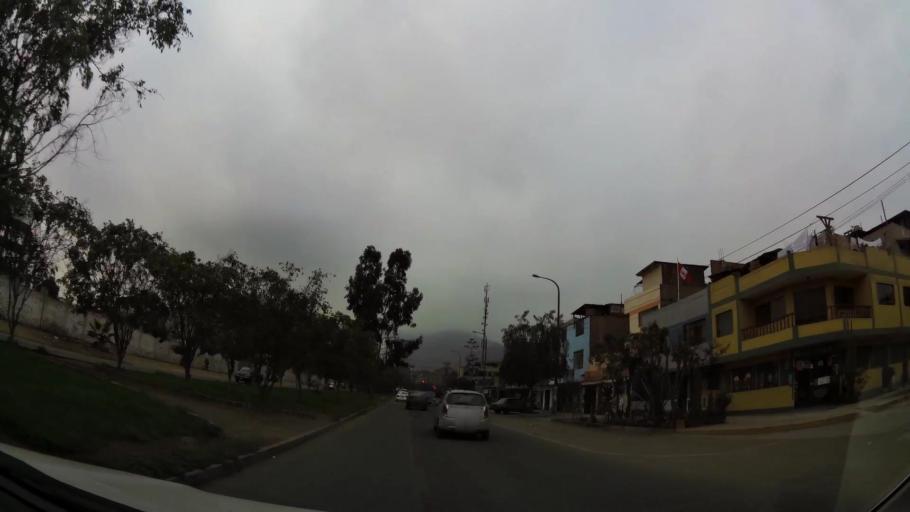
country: PE
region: Lima
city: Lima
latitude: -12.0123
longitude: -76.9997
